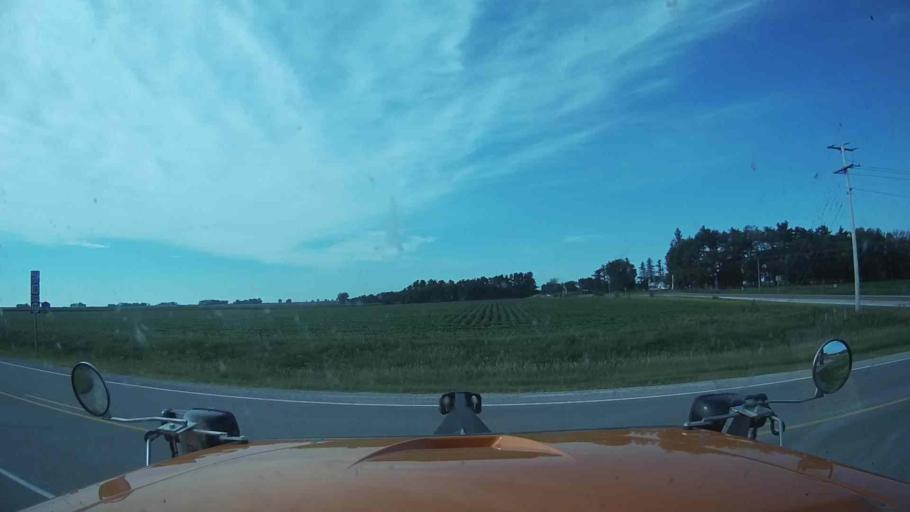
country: US
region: Iowa
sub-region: Cerro Gordo County
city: Rockwell
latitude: 43.0668
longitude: -93.2007
